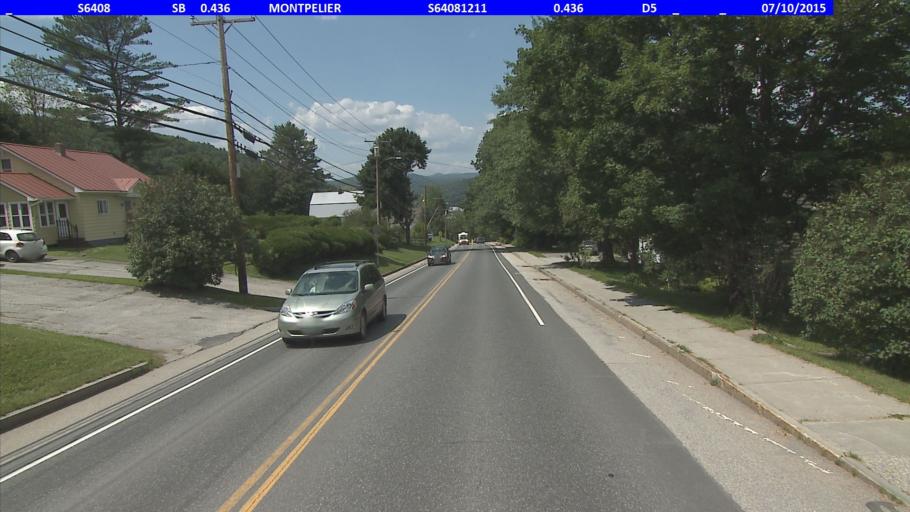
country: US
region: Vermont
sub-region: Washington County
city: Montpelier
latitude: 44.2461
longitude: -72.5670
